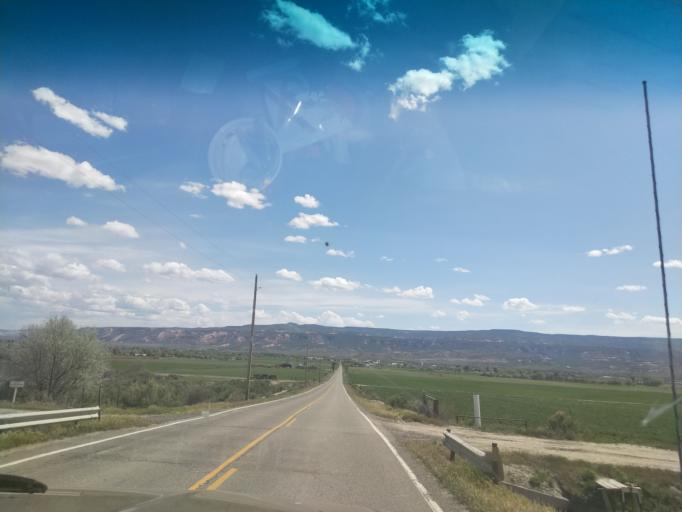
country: US
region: Colorado
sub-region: Mesa County
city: Fruita
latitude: 39.1919
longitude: -108.7571
